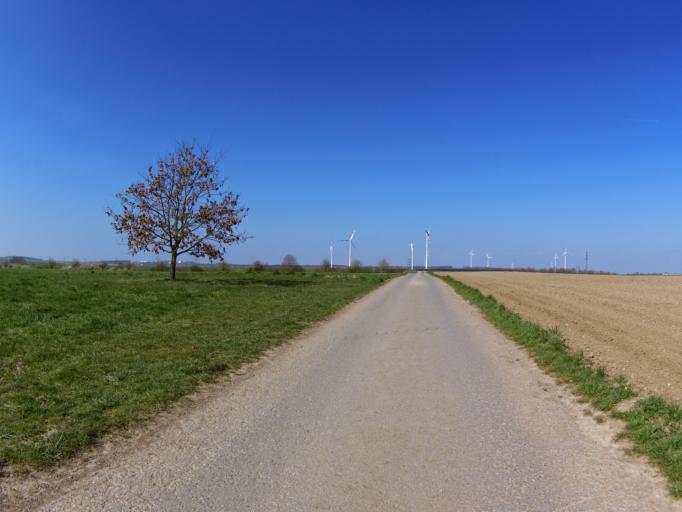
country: DE
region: Bavaria
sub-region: Regierungsbezirk Unterfranken
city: Biebelried
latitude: 49.7387
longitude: 10.1011
